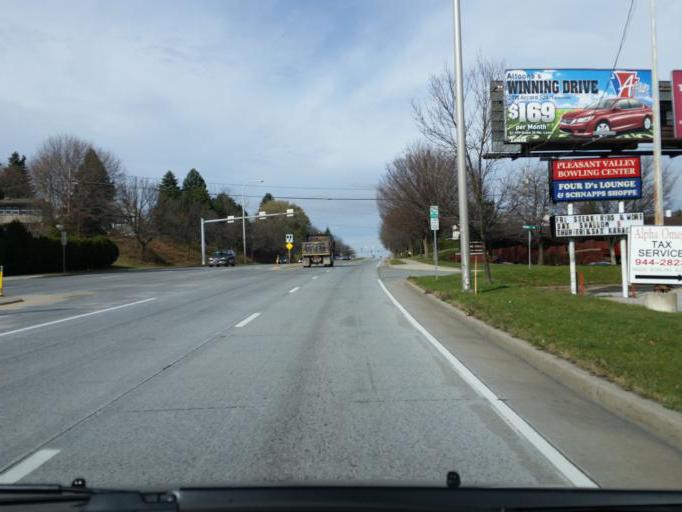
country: US
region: Pennsylvania
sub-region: Blair County
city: Altoona
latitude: 40.5016
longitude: -78.3933
